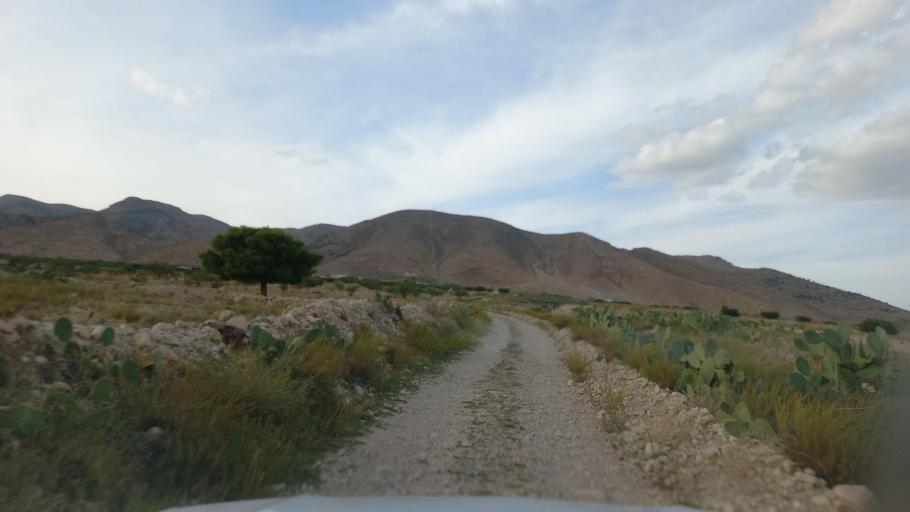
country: TN
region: Al Qasrayn
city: Sbiba
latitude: 35.4463
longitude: 9.0679
